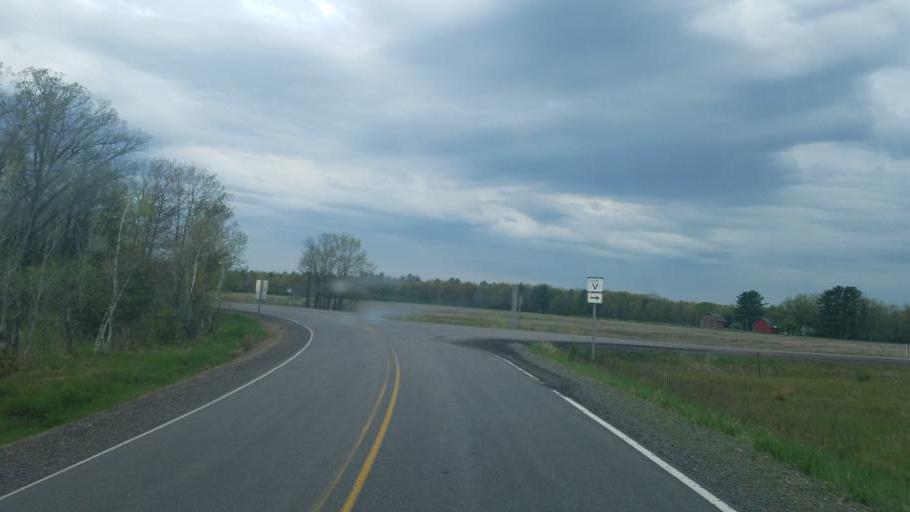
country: US
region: Wisconsin
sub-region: Wood County
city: Marshfield
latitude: 44.4093
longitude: -90.2169
